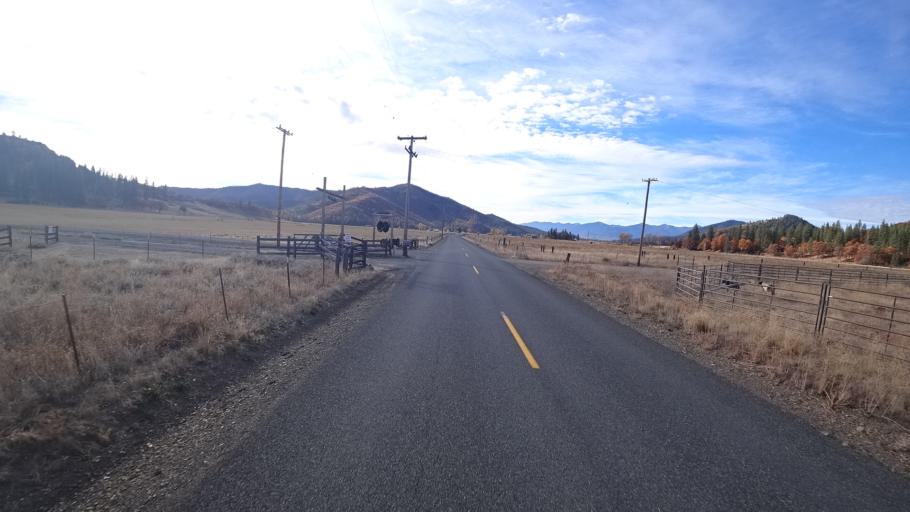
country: US
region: California
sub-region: Siskiyou County
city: Yreka
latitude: 41.6398
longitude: -122.8292
